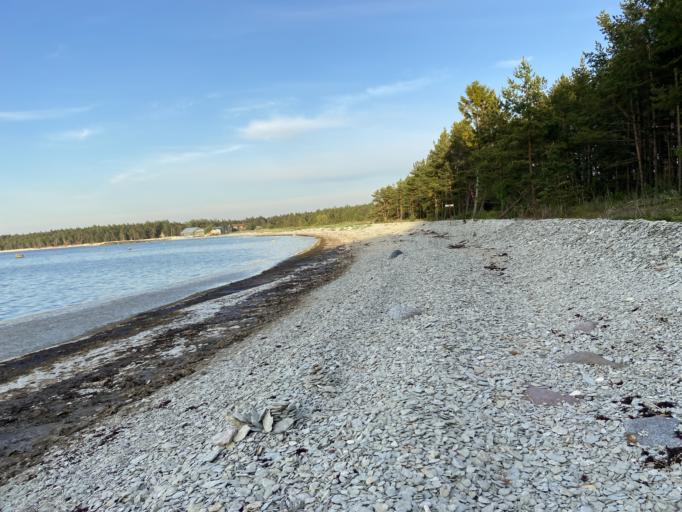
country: EE
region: Harju
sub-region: Paldiski linn
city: Paldiski
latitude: 59.2711
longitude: 23.7352
